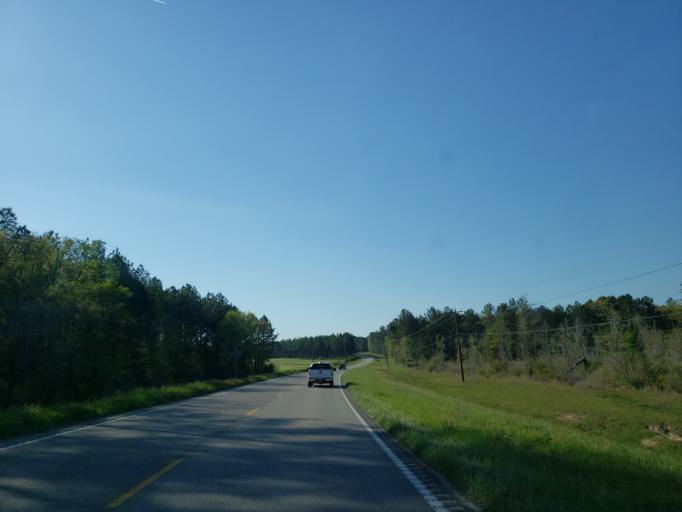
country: US
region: Mississippi
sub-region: Perry County
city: Richton
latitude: 31.4729
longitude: -89.0019
